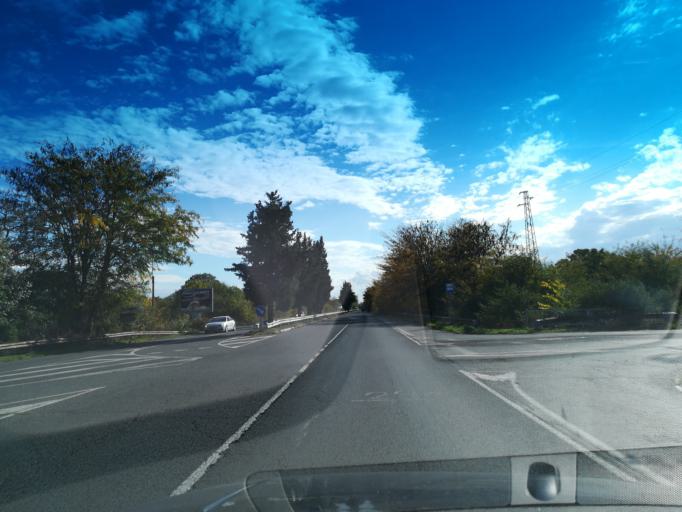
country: BG
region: Stara Zagora
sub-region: Obshtina Stara Zagora
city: Stara Zagora
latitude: 42.3886
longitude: 25.6477
